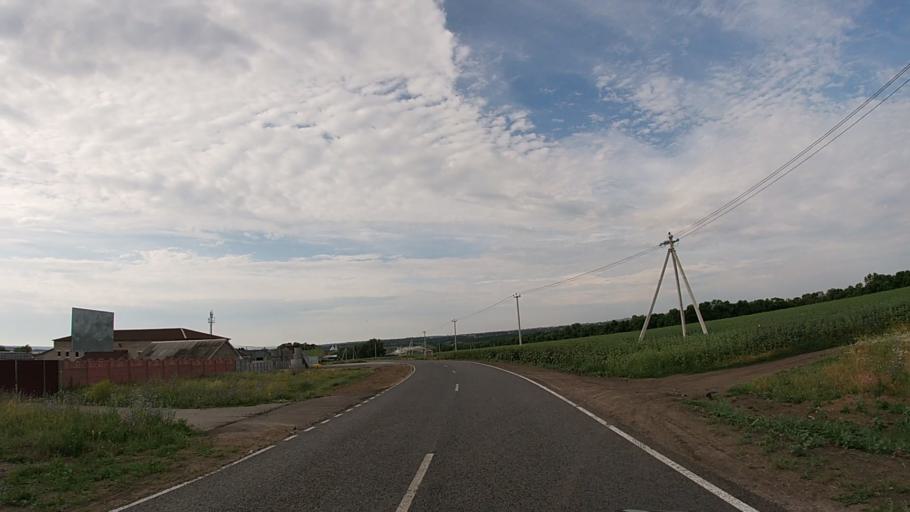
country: RU
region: Belgorod
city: Severnyy
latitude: 50.7219
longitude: 36.5845
